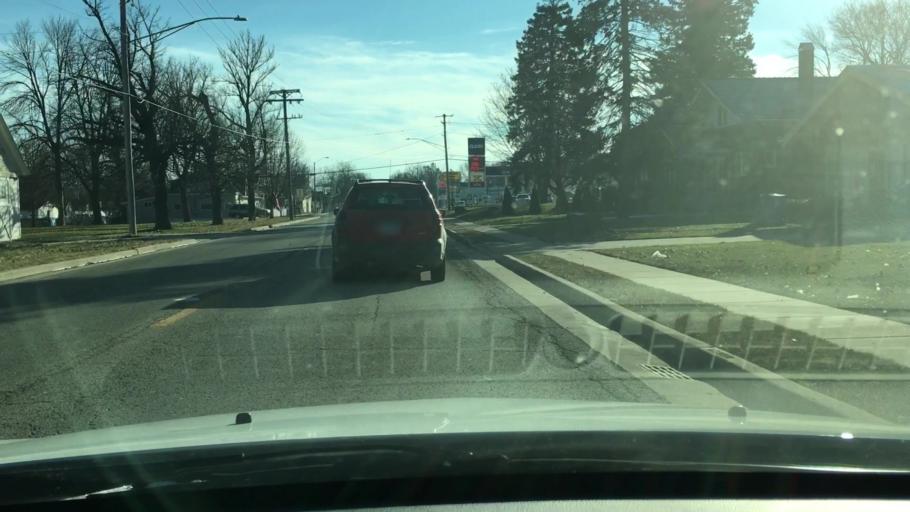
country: US
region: Illinois
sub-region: LaSalle County
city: Mendota
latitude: 41.5502
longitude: -89.1277
